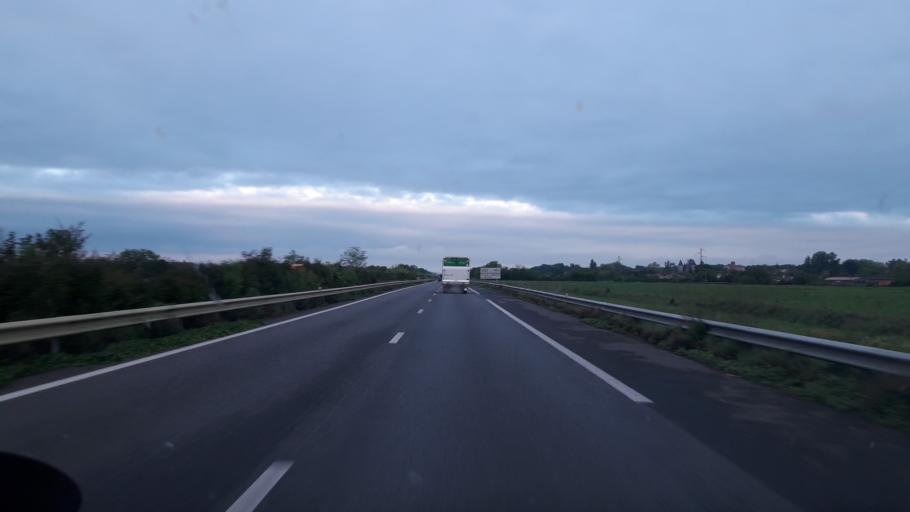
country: FR
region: Midi-Pyrenees
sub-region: Departement de la Haute-Garonne
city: Rieux-Volvestre
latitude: 43.2827
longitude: 1.1535
